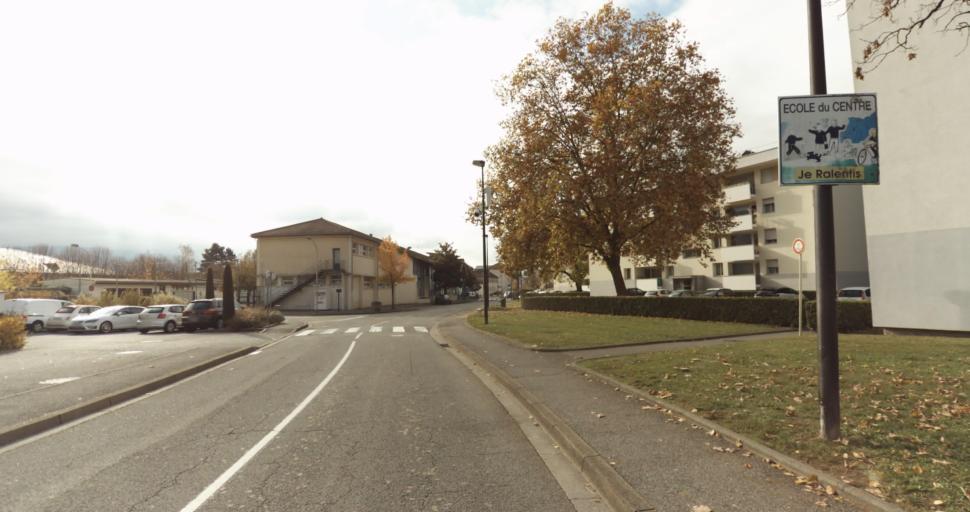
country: FR
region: Rhone-Alpes
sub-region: Departement de la Haute-Savoie
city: Meythet
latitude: 45.9170
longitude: 6.0942
